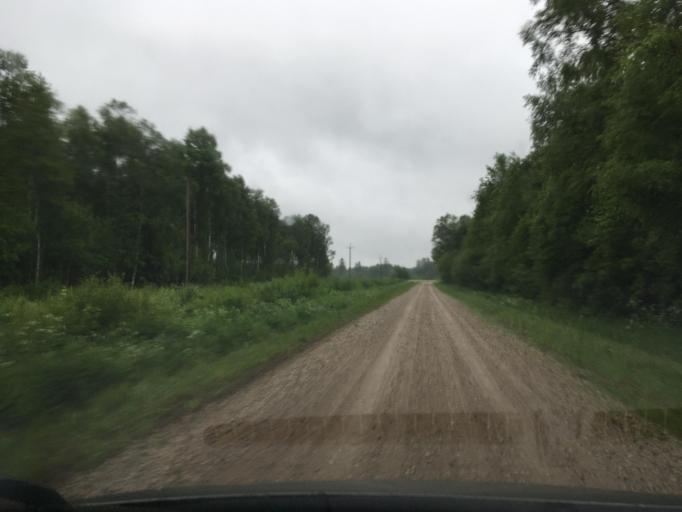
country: EE
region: Laeaene
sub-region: Lihula vald
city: Lihula
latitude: 58.5985
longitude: 23.8388
